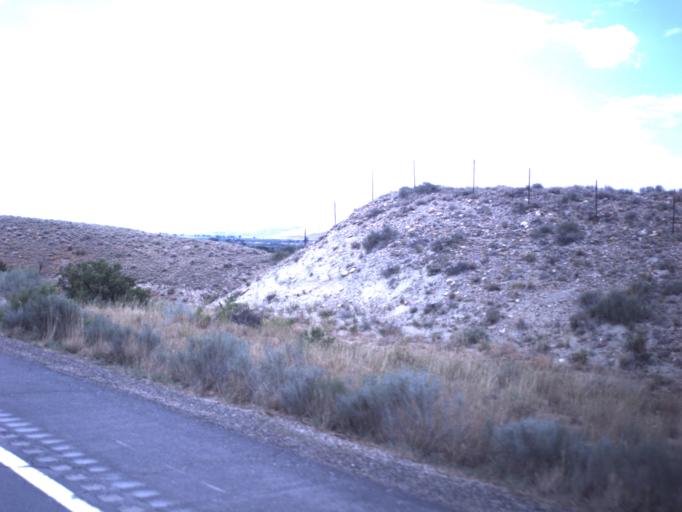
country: US
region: Utah
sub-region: Duchesne County
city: Duchesne
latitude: 40.1575
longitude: -110.2573
